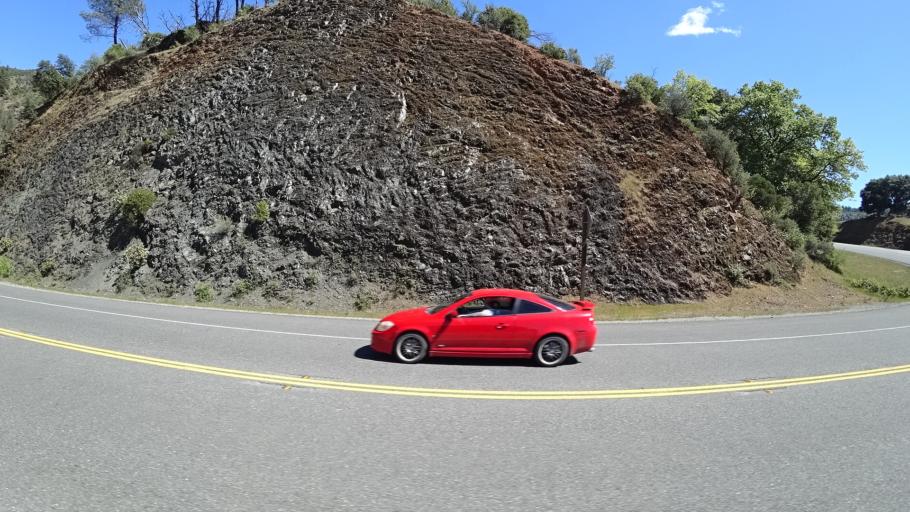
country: US
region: California
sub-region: Trinity County
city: Weaverville
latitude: 40.7389
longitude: -123.0006
